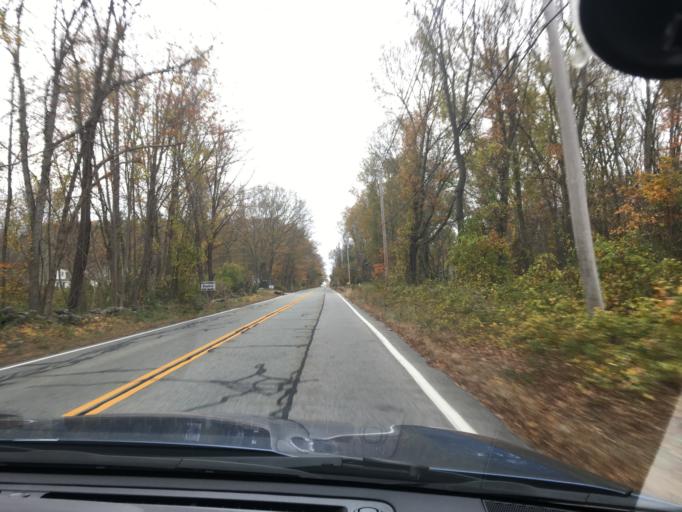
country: US
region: Rhode Island
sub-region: Providence County
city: North Scituate
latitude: 41.8046
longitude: -71.6585
